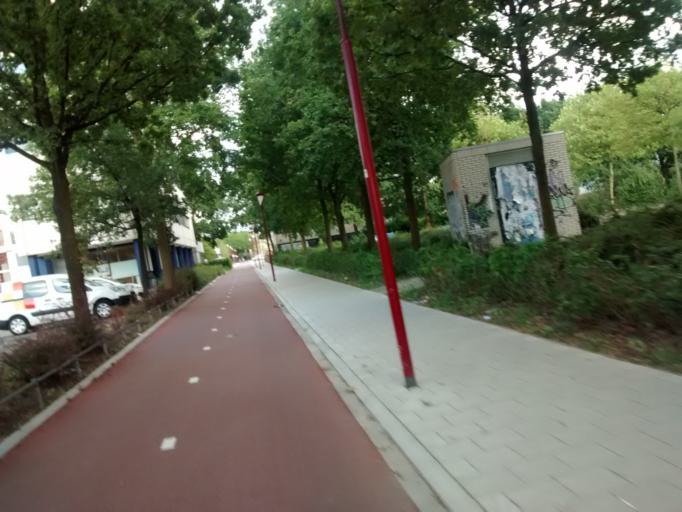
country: NL
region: Utrecht
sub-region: Gemeente Nieuwegein
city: Nieuwegein
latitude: 52.0278
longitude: 5.0904
